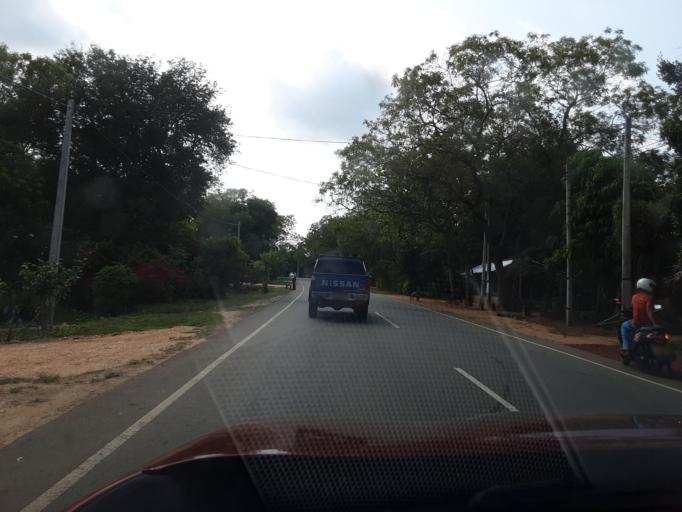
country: LK
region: Uva
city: Haputale
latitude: 6.3580
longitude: 81.1858
